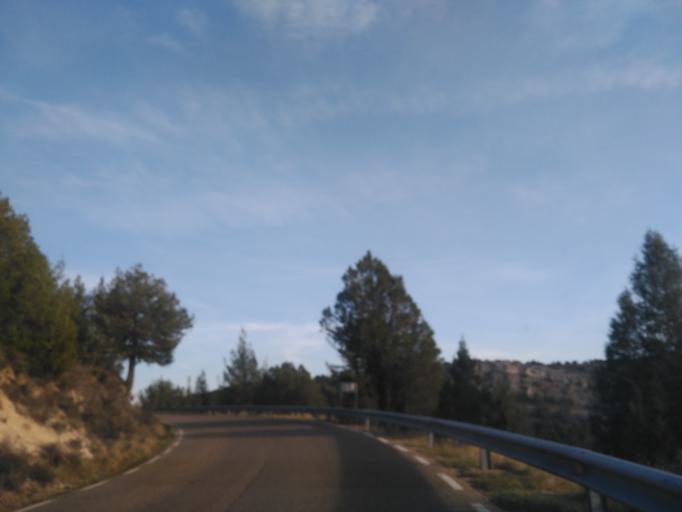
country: ES
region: Castille and Leon
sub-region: Provincia de Soria
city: Ucero
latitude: 41.7275
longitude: -3.0435
